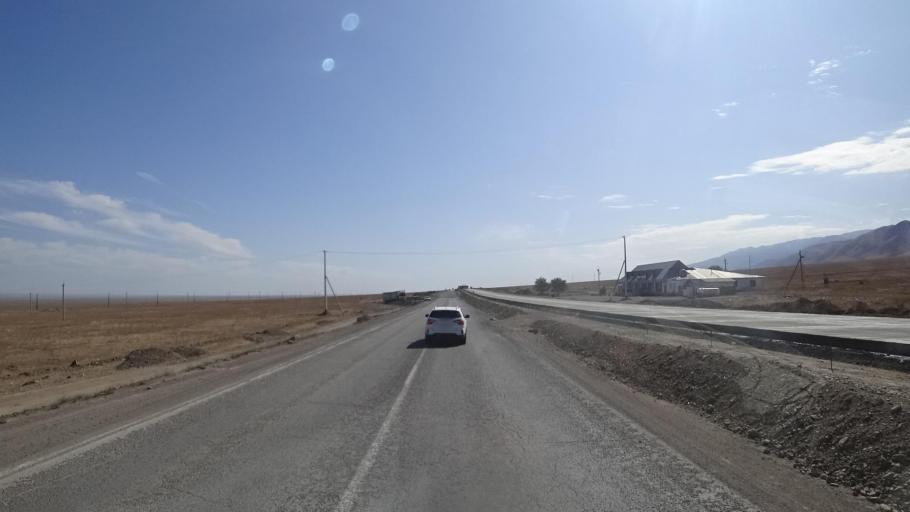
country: KG
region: Chuy
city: Ivanovka
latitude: 43.3852
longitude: 75.1672
